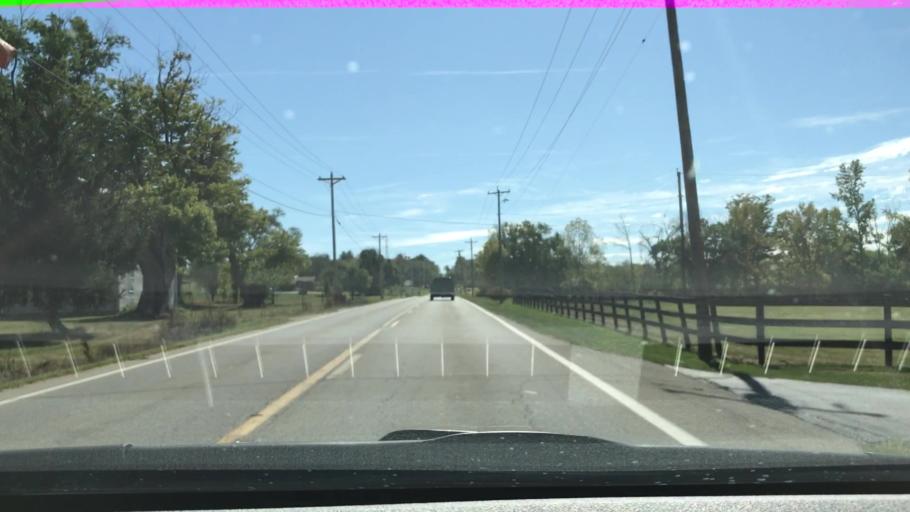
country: US
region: Ohio
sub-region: Butler County
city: Hamilton
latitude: 39.4567
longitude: -84.6256
